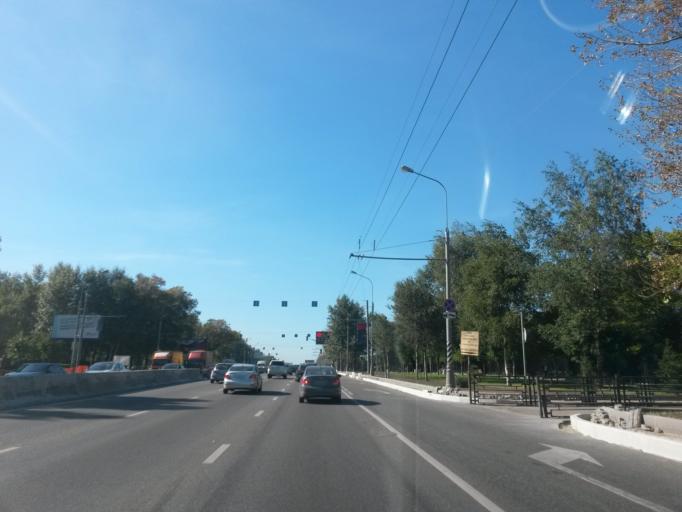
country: RU
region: Moscow
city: Nagornyy
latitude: 55.6574
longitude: 37.6441
